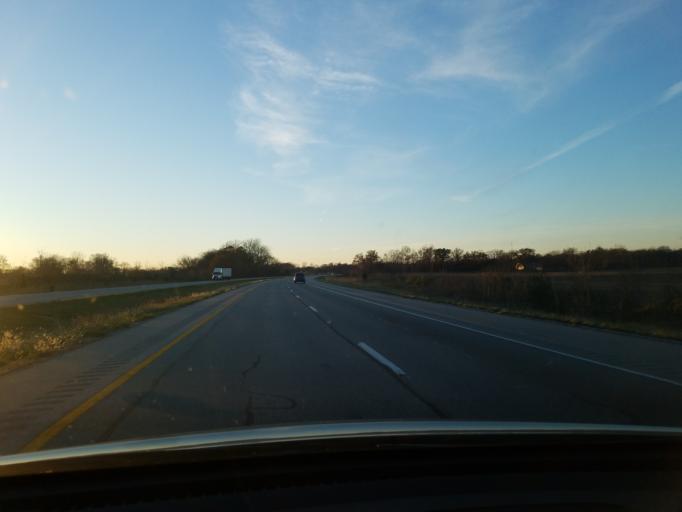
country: US
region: Indiana
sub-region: Posey County
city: Poseyville
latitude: 38.1847
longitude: -87.8179
